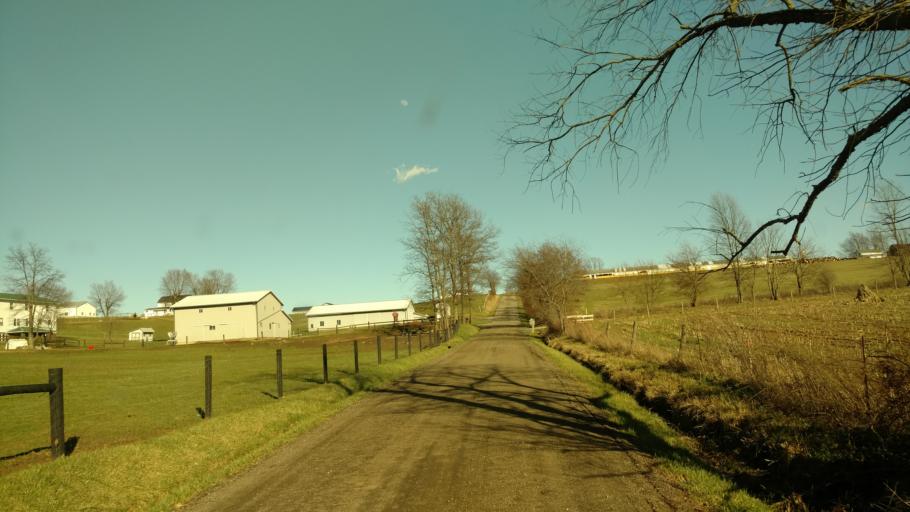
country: US
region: Ohio
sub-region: Tuscarawas County
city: Sugarcreek
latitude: 40.6120
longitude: -81.7518
